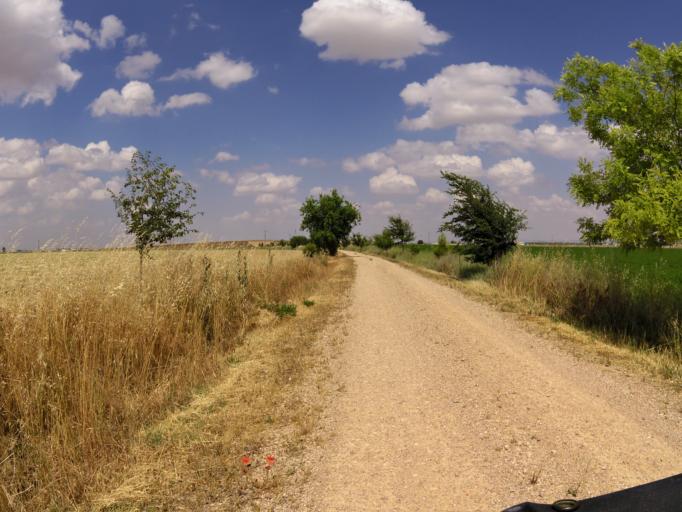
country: ES
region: Castille-La Mancha
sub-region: Provincia de Albacete
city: Pozuelo
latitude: 38.9132
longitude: -2.0157
